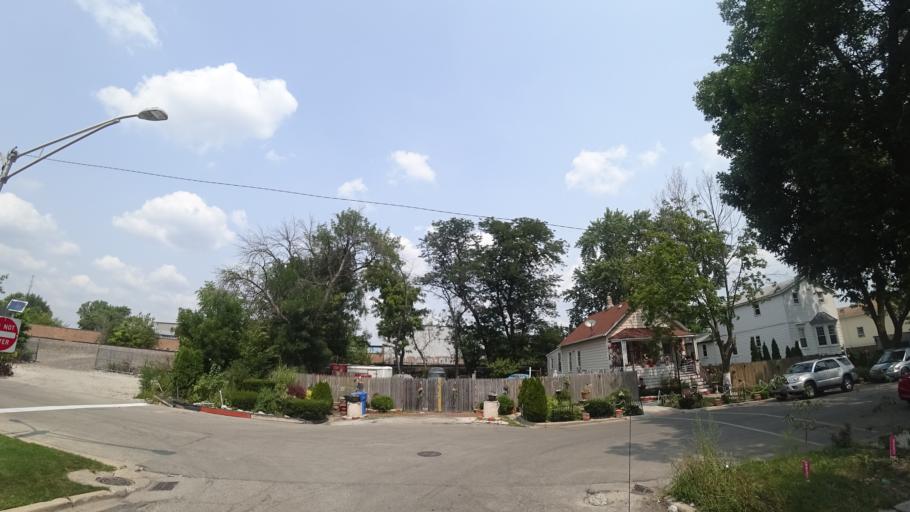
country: US
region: Illinois
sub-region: Cook County
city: Cicero
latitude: 41.8467
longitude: -87.7311
